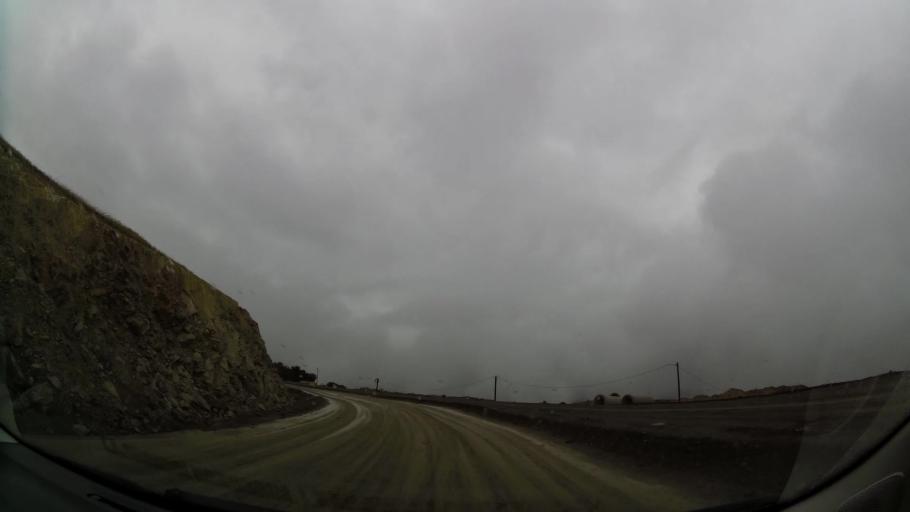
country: MA
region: Taza-Al Hoceima-Taounate
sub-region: Taza
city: Ajdir
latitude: 34.9007
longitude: -3.7862
